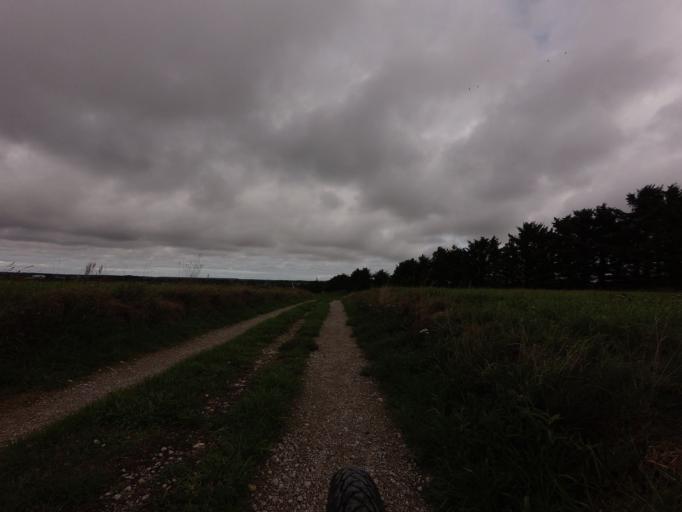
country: DK
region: North Denmark
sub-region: Hjorring Kommune
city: Hjorring
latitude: 57.4724
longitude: 9.9803
